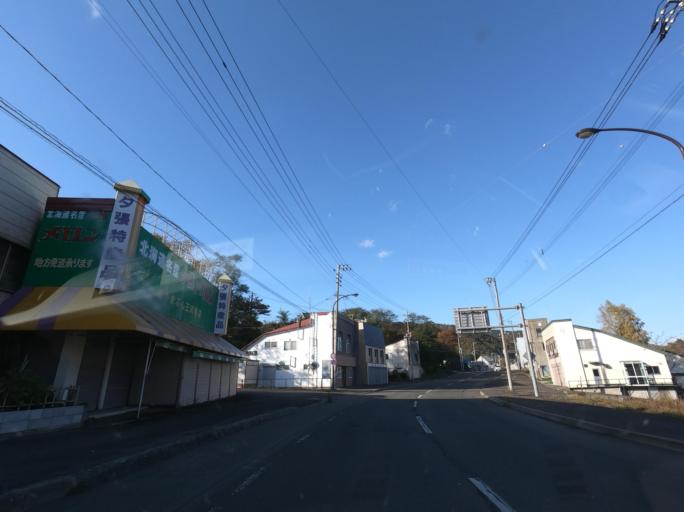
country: JP
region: Hokkaido
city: Iwamizawa
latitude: 43.0396
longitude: 141.9621
